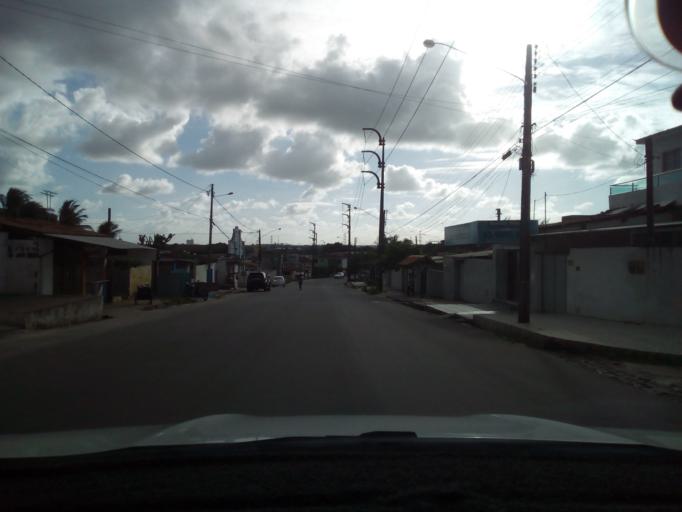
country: BR
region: Paraiba
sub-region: Joao Pessoa
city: Joao Pessoa
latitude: -7.1846
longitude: -34.8855
